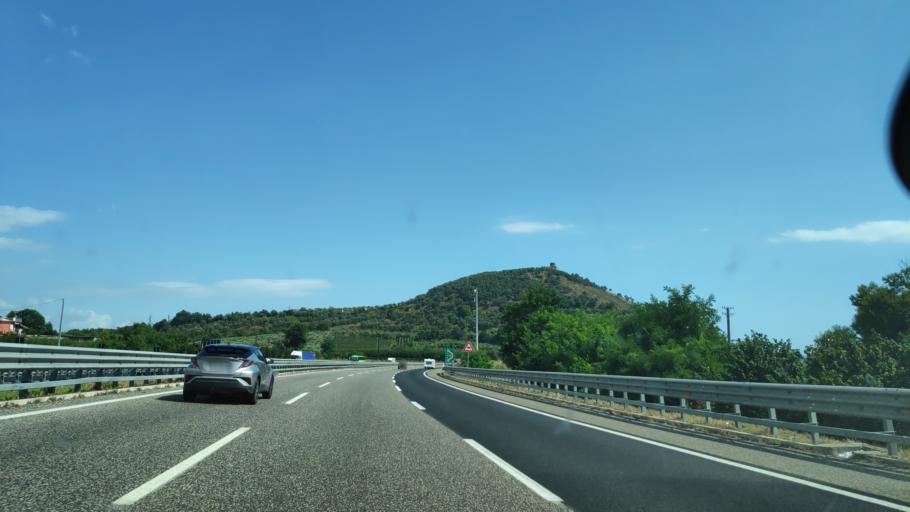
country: IT
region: Campania
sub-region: Provincia di Salerno
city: Pezzano-Filetta
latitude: 40.6837
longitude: 14.8547
